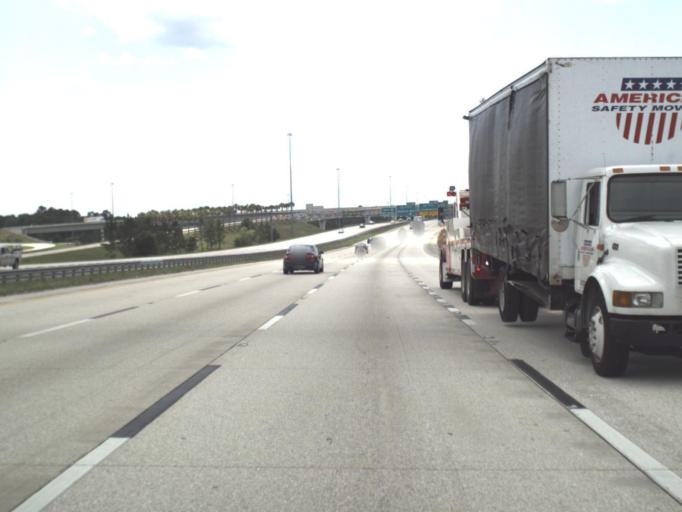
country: US
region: Florida
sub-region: Saint Johns County
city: Fruit Cove
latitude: 30.1665
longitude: -81.5474
